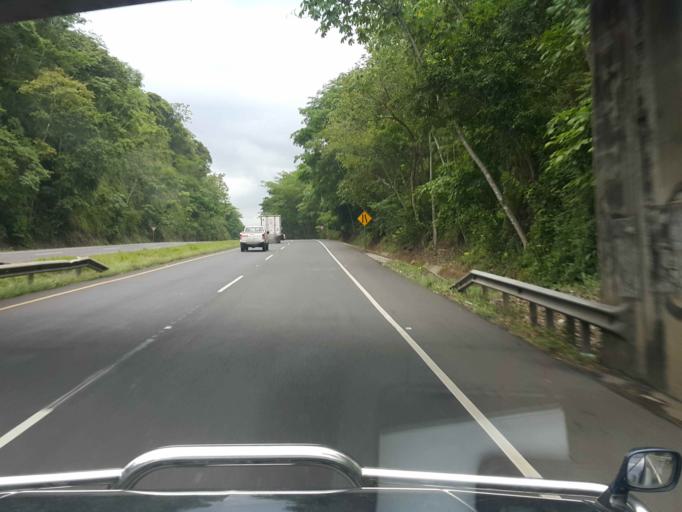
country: CR
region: Alajuela
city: Orotina
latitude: 9.9002
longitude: -84.5422
